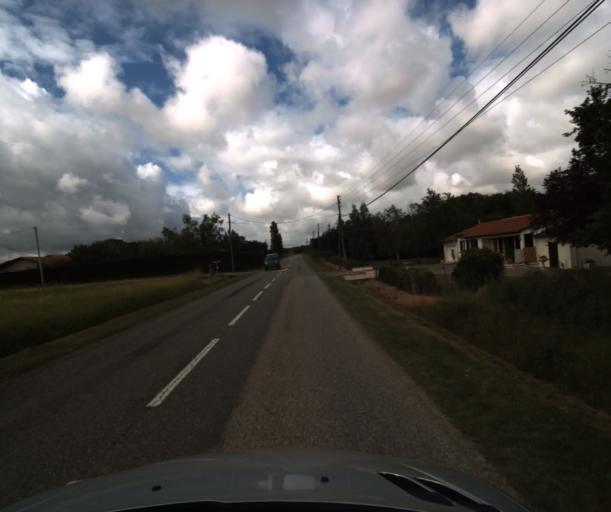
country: FR
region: Midi-Pyrenees
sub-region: Departement du Tarn-et-Garonne
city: Lavit
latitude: 43.9749
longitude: 0.9536
